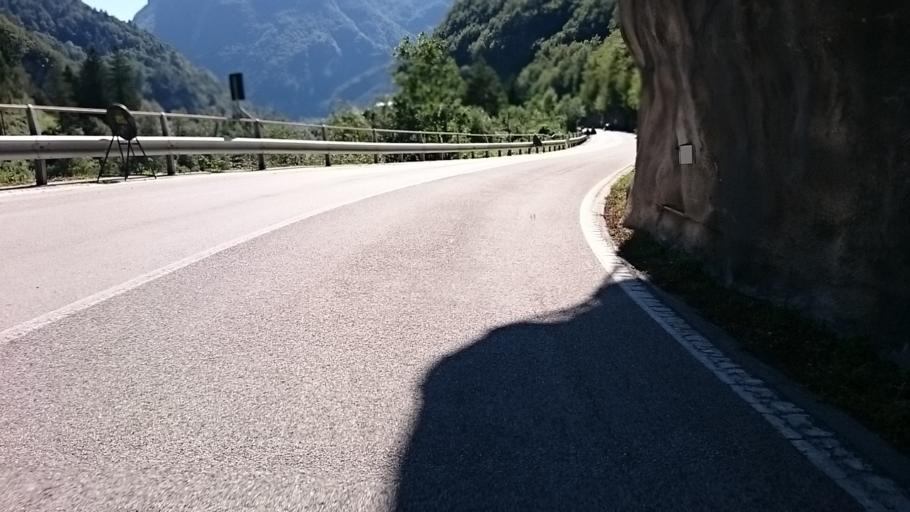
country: IT
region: Veneto
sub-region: Provincia di Belluno
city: Ospitale di Cadore
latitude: 46.3330
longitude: 12.3302
